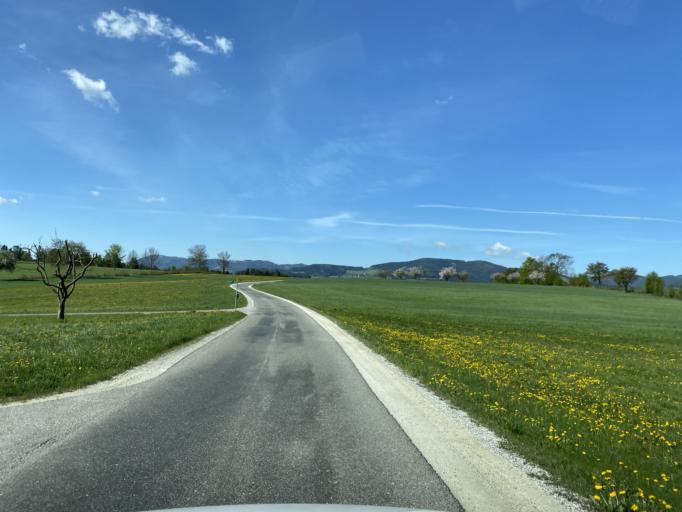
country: AT
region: Styria
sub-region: Politischer Bezirk Weiz
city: Strallegg
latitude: 47.3719
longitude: 15.7171
